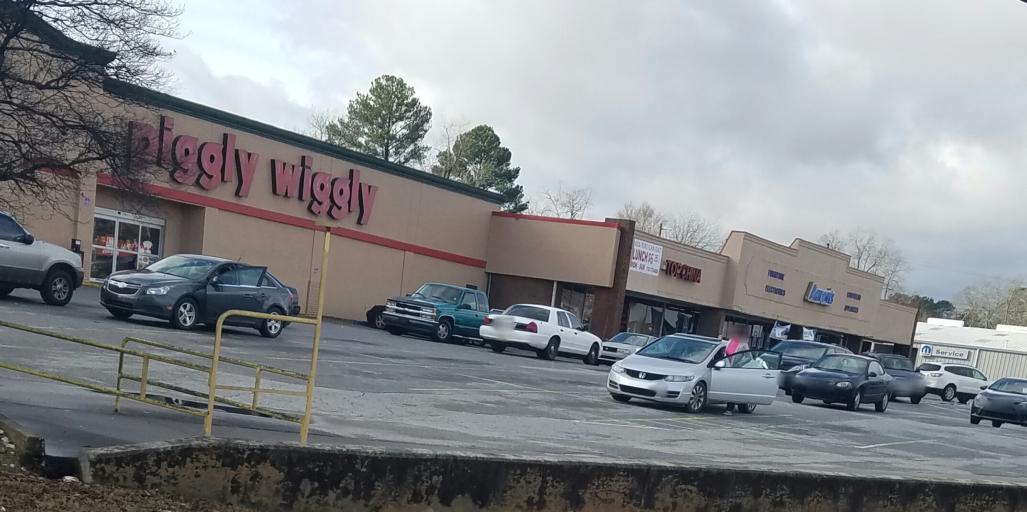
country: US
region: Georgia
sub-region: Butts County
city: Jackson
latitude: 33.2928
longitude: -83.9531
